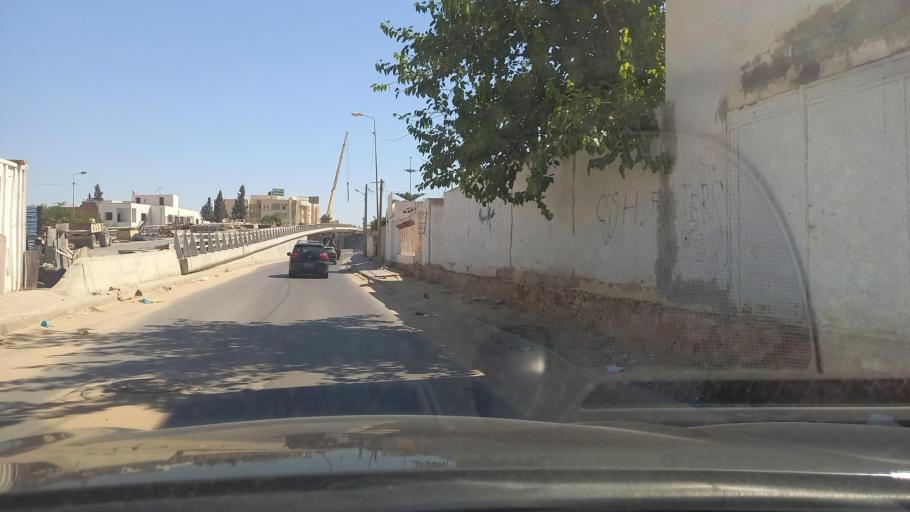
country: TN
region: Safaqis
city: Sfax
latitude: 34.7441
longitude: 10.7251
